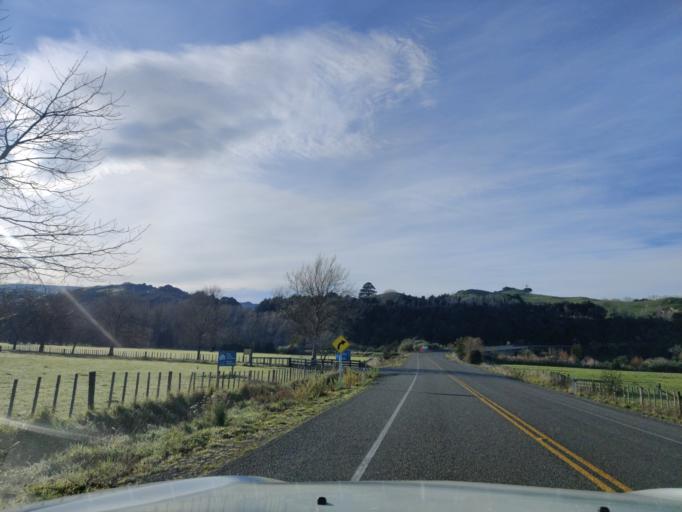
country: NZ
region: Manawatu-Wanganui
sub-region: Palmerston North City
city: Palmerston North
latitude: -40.2804
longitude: 175.7674
